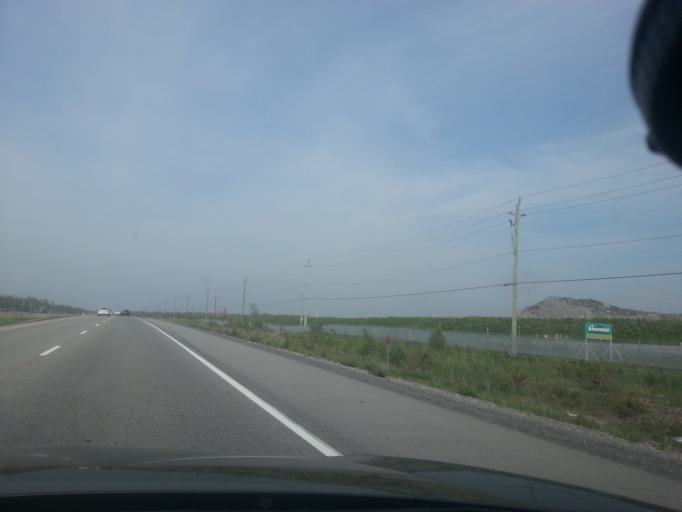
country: CA
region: Ontario
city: Bells Corners
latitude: 45.2328
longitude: -75.9901
